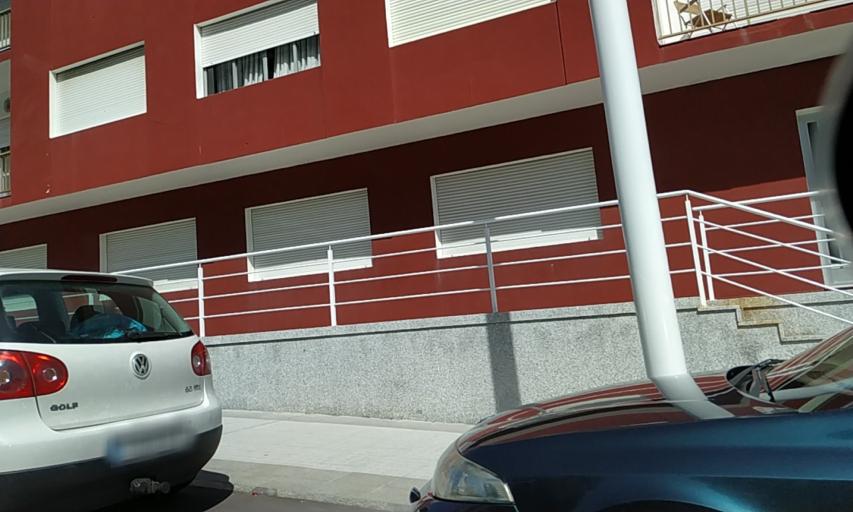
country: ES
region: Galicia
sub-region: Provincia de Pontevedra
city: Sanxenxo
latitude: 42.4050
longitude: -8.8126
